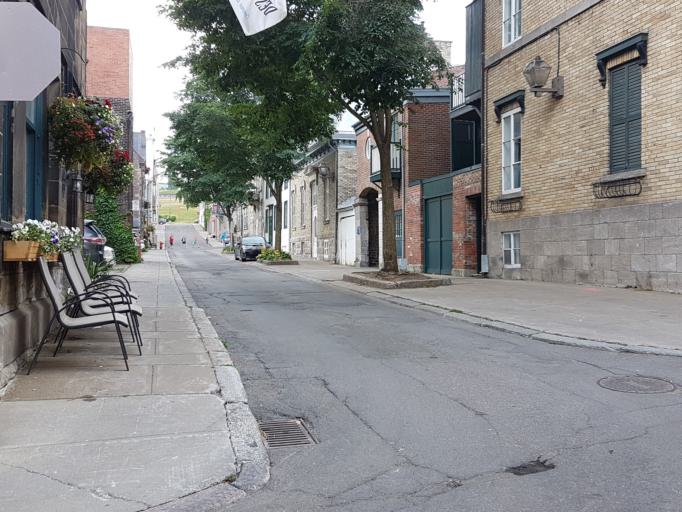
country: CA
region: Quebec
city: Quebec
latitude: 46.8109
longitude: -71.2068
